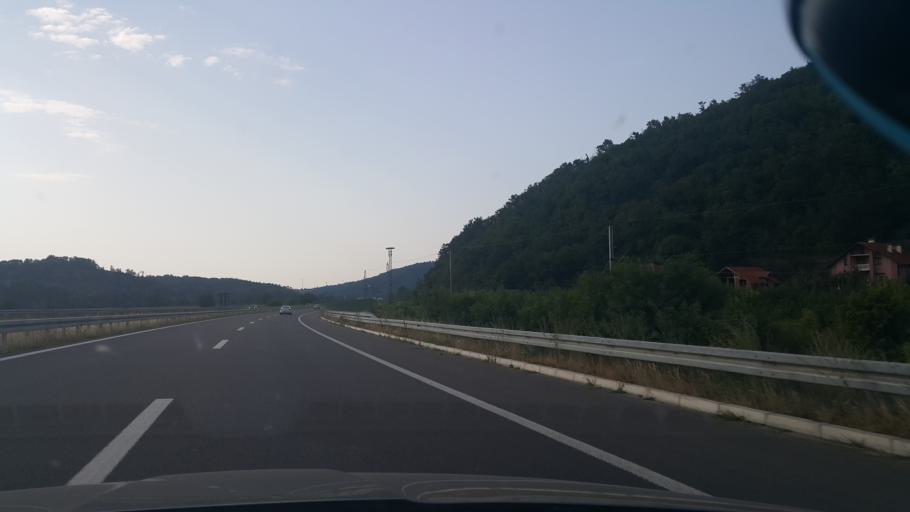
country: RS
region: Central Serbia
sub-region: Jablanicki Okrug
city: Vlasotince
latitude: 42.8967
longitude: 22.0532
